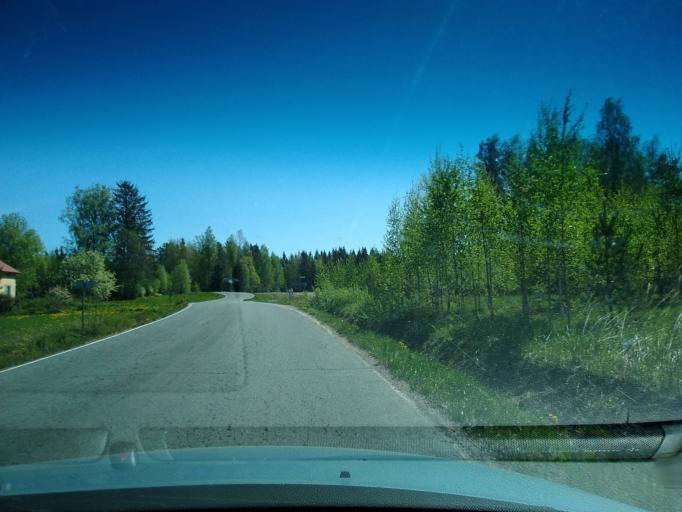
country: FI
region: Haeme
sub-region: Haemeenlinna
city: Renko
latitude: 60.7735
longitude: 24.1171
